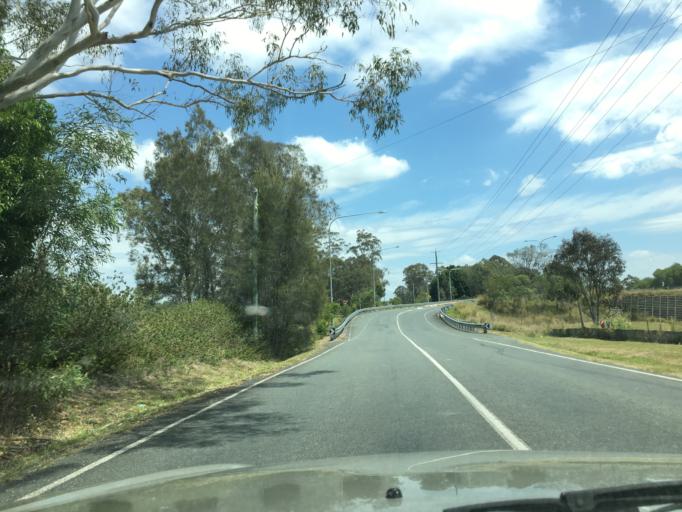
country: AU
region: Queensland
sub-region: Logan
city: Waterford West
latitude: -27.7095
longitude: 153.1462
